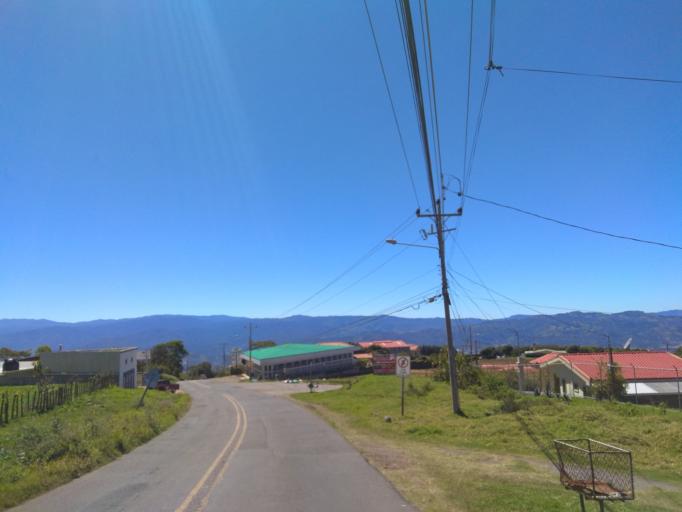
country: CR
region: Cartago
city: Cot
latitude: 9.9236
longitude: -83.9163
